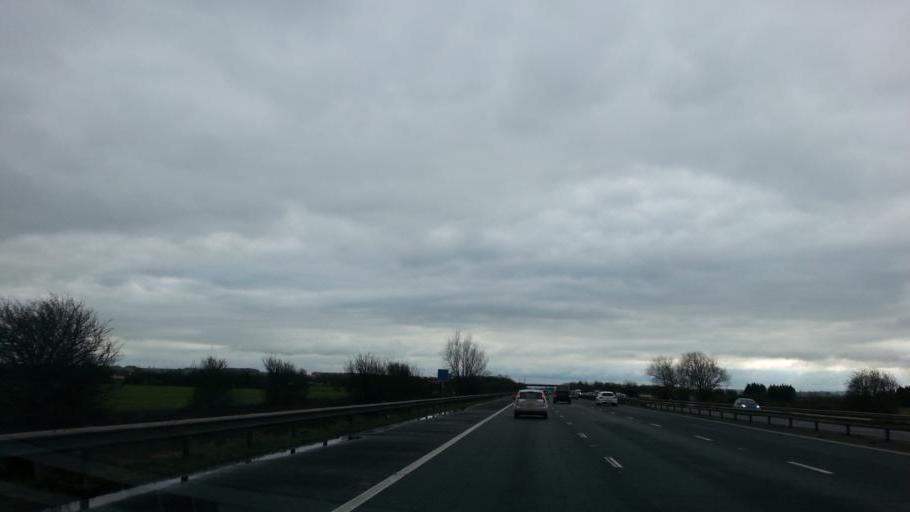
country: GB
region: England
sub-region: Somerset
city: Highbridge
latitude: 51.2034
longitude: -2.9670
